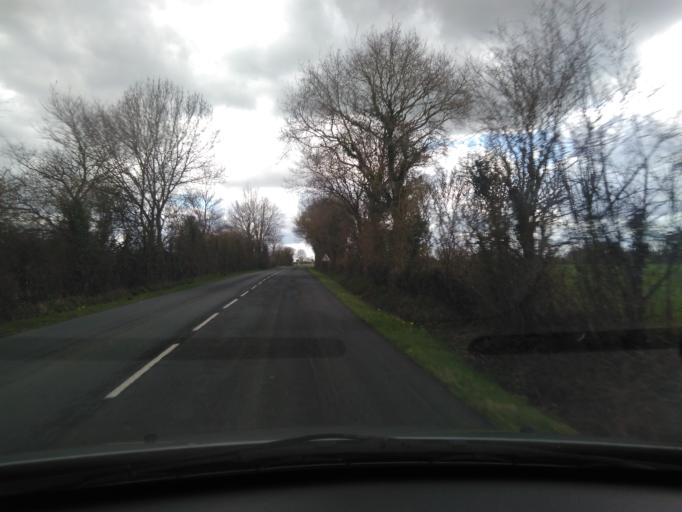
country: FR
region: Pays de la Loire
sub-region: Departement de la Vendee
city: Les Essarts
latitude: 46.7522
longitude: -1.2144
